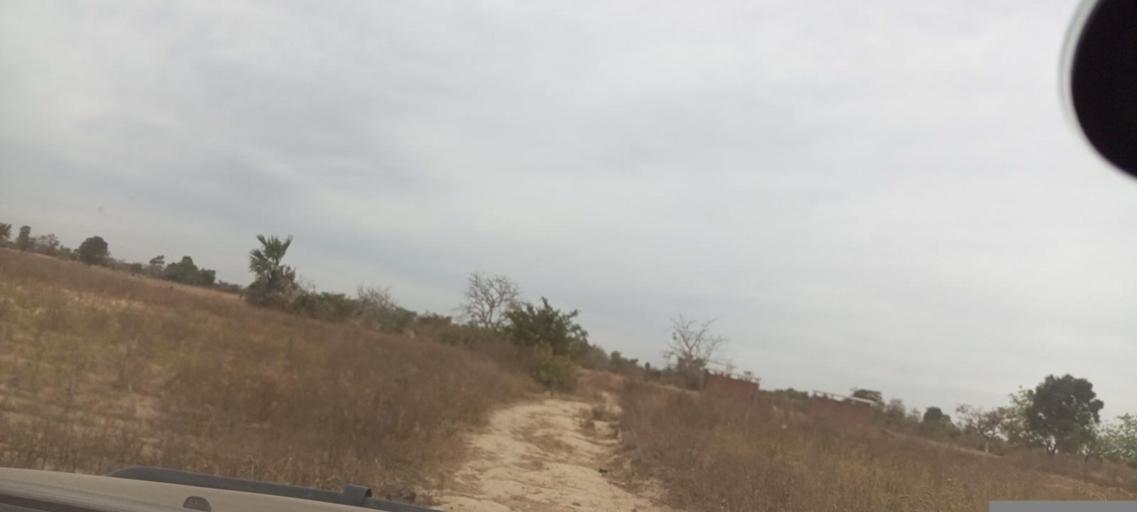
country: ML
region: Koulikoro
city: Kati
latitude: 12.7495
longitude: -8.3605
